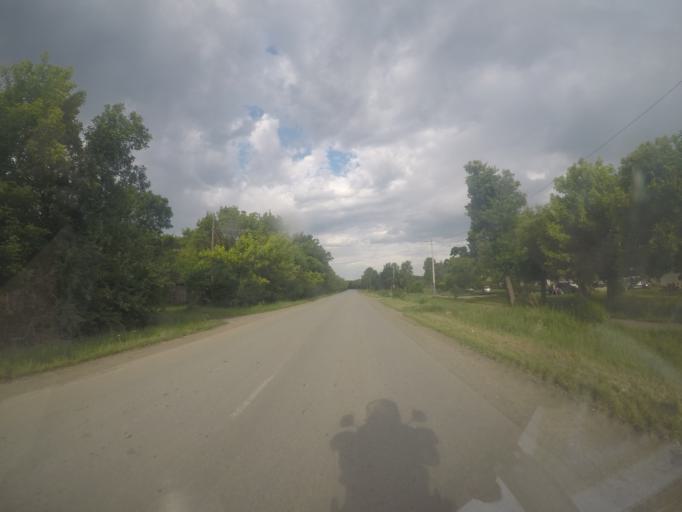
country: RS
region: Central Serbia
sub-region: Belgrade
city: Zemun
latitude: 44.9099
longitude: 20.4287
